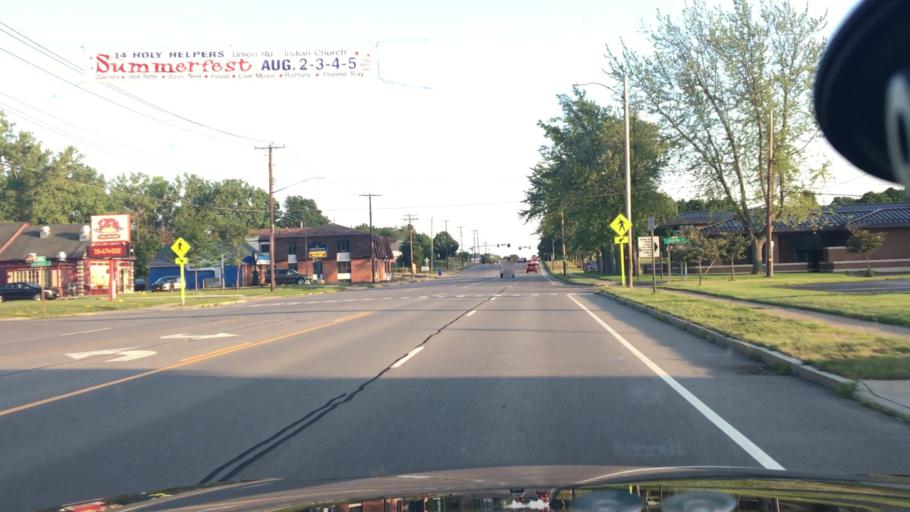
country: US
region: New York
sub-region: Erie County
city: West Seneca
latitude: 42.8363
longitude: -78.7541
